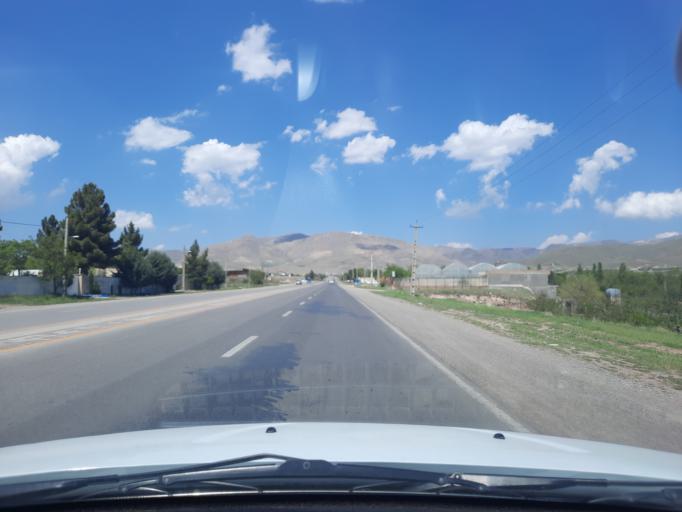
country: IR
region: Qazvin
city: Alvand
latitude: 36.3084
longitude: 50.1448
